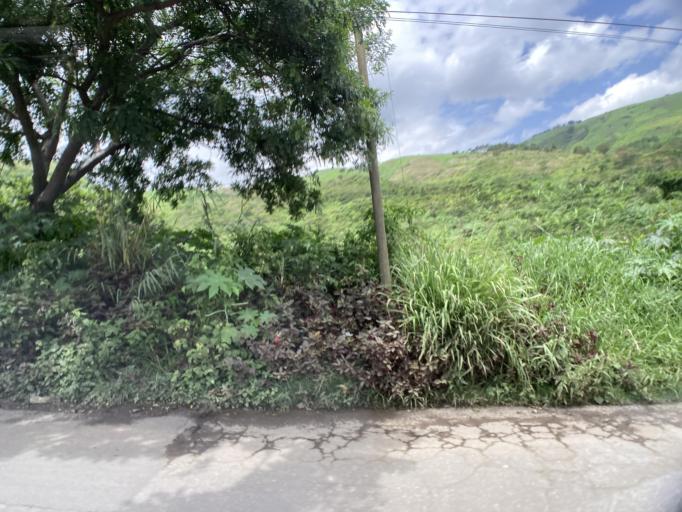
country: GT
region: Guatemala
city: Villa Canales
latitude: 14.4541
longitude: -90.5707
